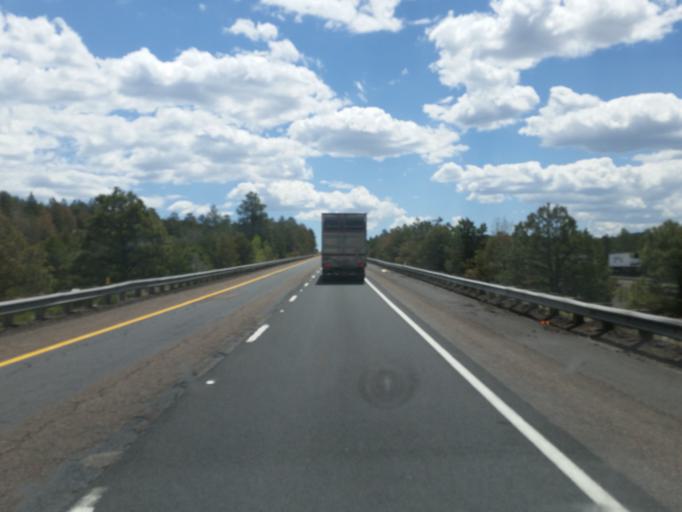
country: US
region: Arizona
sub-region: Coconino County
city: Parks
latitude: 35.2549
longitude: -111.9192
